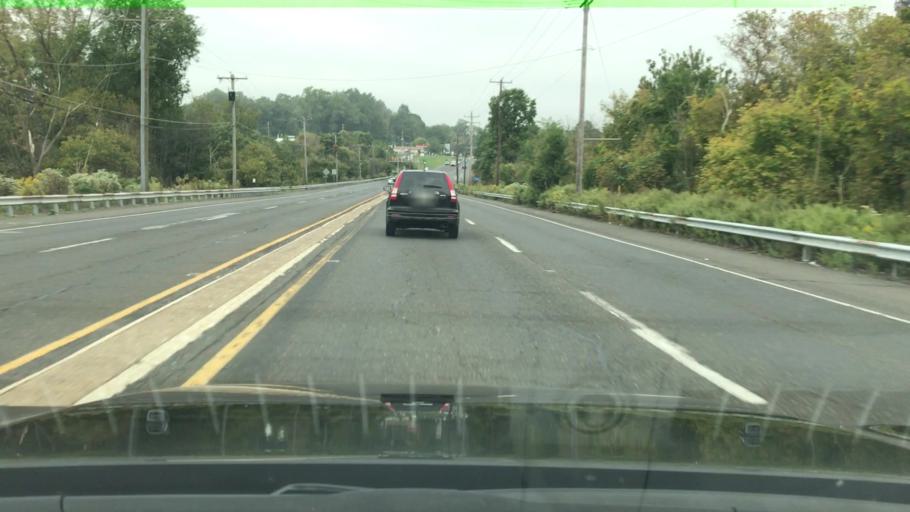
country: US
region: Pennsylvania
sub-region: Bucks County
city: Woodbourne
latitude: 40.1769
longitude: -74.8976
